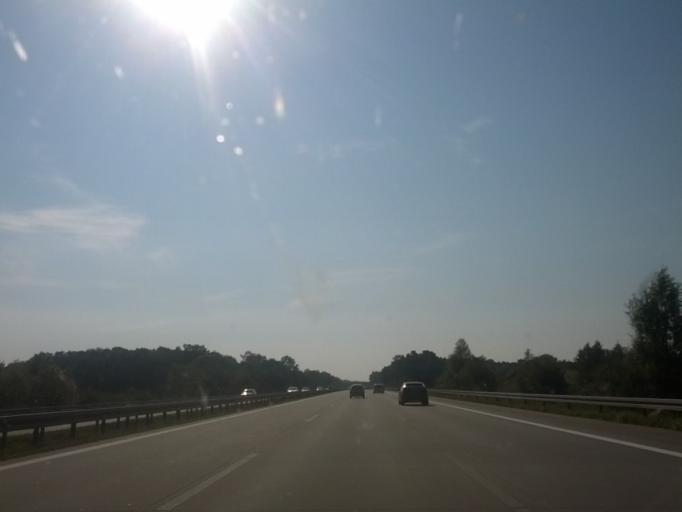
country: DE
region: Brandenburg
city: Ahrensfelde
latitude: 52.5881
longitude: 13.6256
